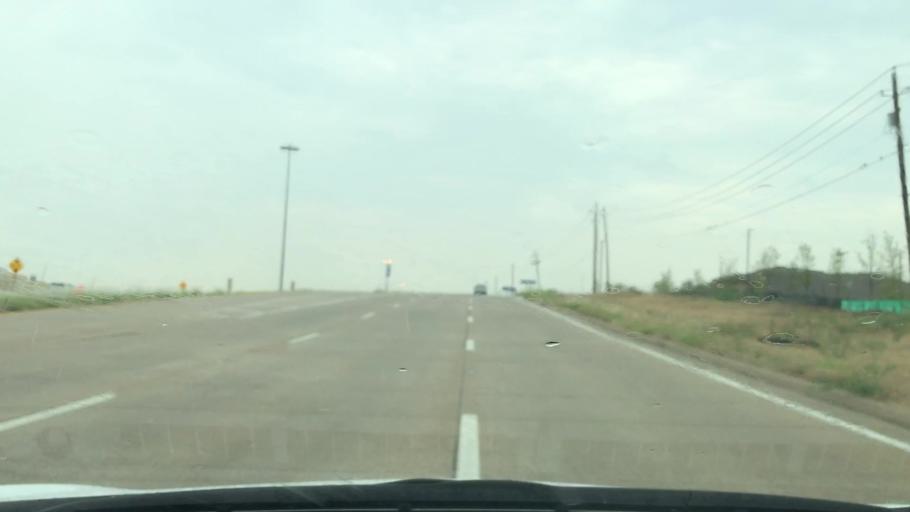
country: US
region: Texas
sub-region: Dallas County
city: Irving
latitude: 32.8720
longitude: -96.9953
